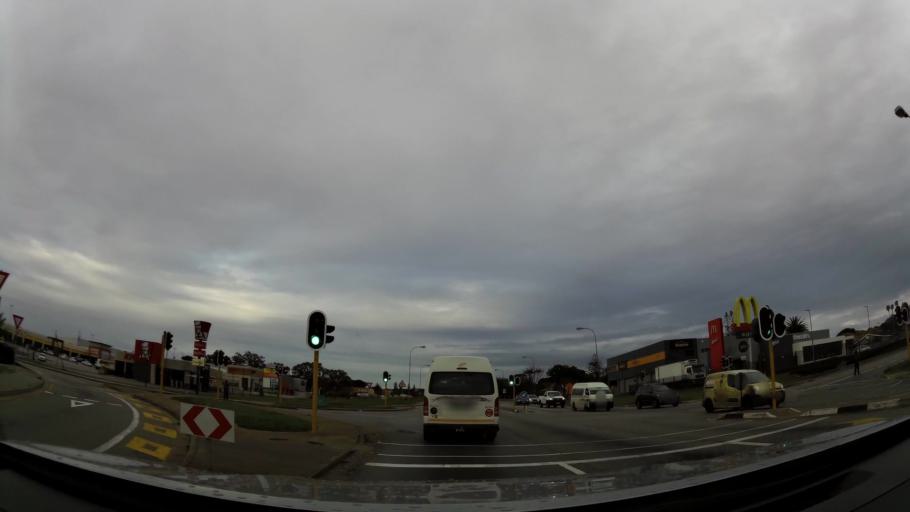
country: ZA
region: Eastern Cape
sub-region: Nelson Mandela Bay Metropolitan Municipality
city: Port Elizabeth
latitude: -33.9838
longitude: 25.5531
